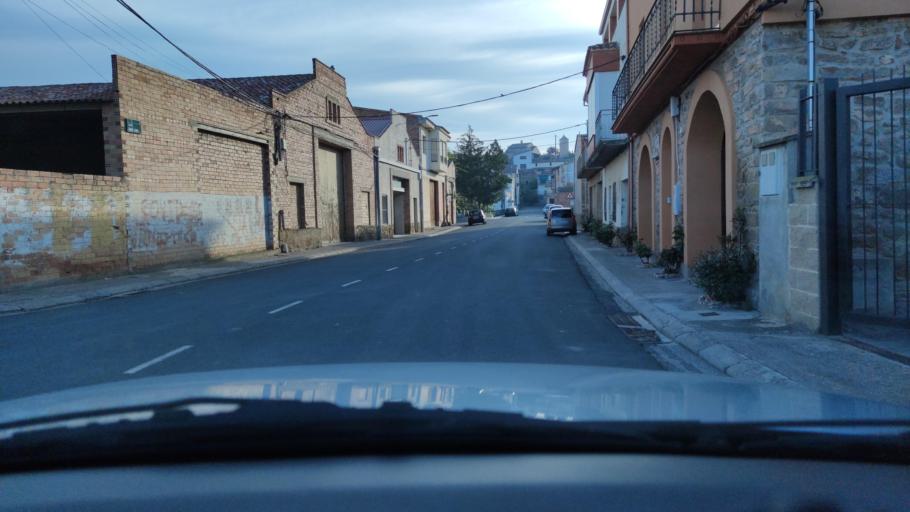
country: ES
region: Catalonia
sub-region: Provincia de Lleida
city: Agramunt
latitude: 41.7933
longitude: 1.0483
